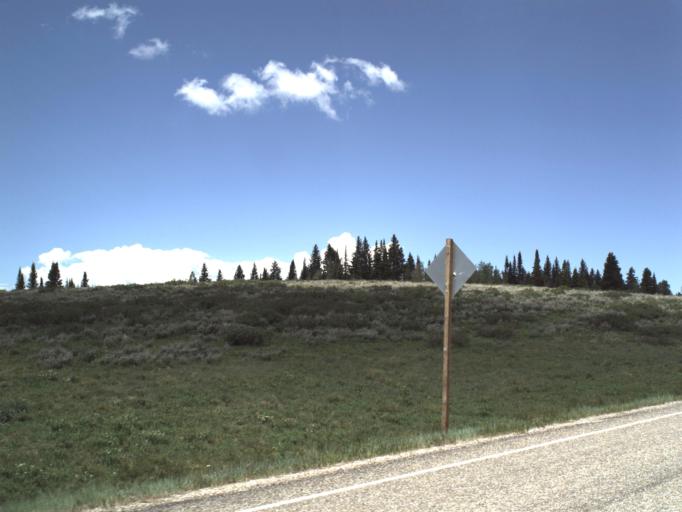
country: US
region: Utah
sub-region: Weber County
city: Wolf Creek
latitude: 41.4414
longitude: -111.5058
